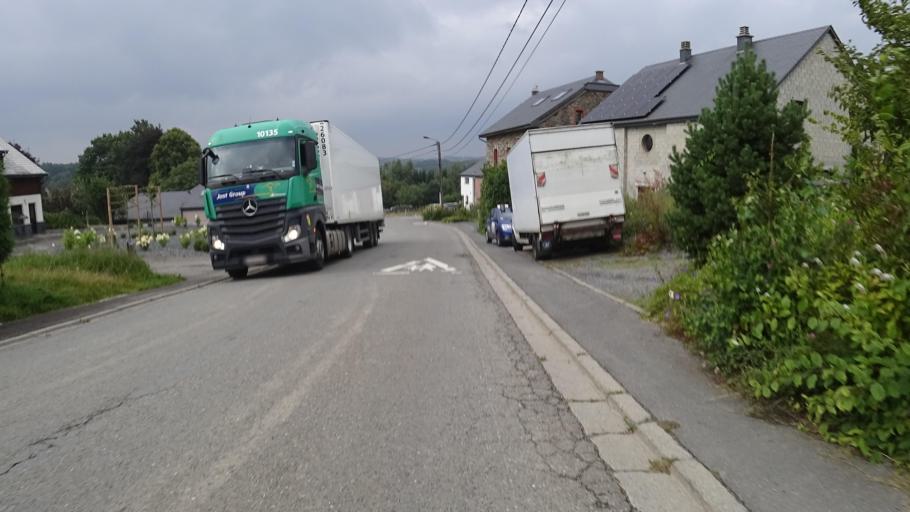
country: BE
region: Wallonia
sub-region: Province du Luxembourg
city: Chiny
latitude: 49.8179
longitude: 5.3282
